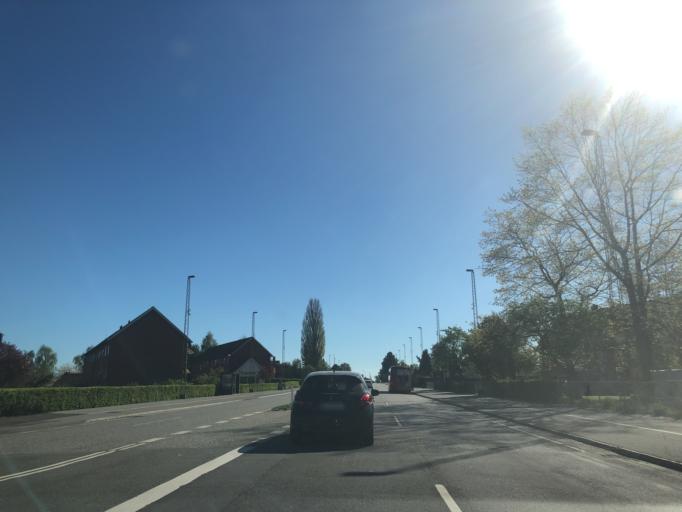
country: DK
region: Zealand
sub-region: Koge Kommune
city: Koge
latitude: 55.4463
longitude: 12.1722
